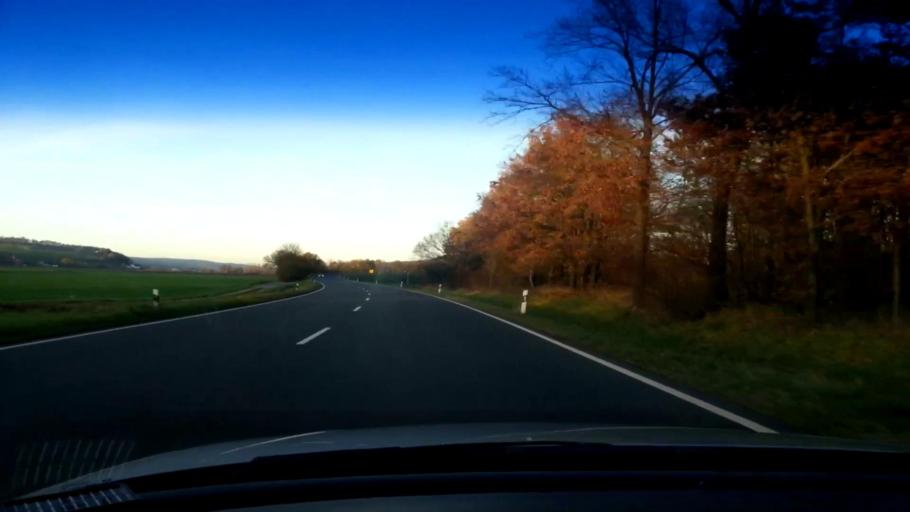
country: DE
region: Bavaria
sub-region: Upper Franconia
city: Rattelsdorf
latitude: 50.0389
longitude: 10.8826
